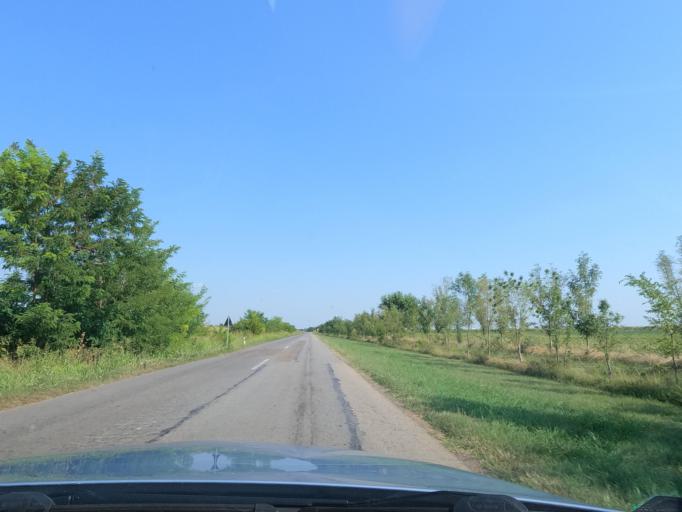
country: RS
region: Autonomna Pokrajina Vojvodina
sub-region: Juznobacki Okrug
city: Becej
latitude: 45.6439
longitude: 19.9898
